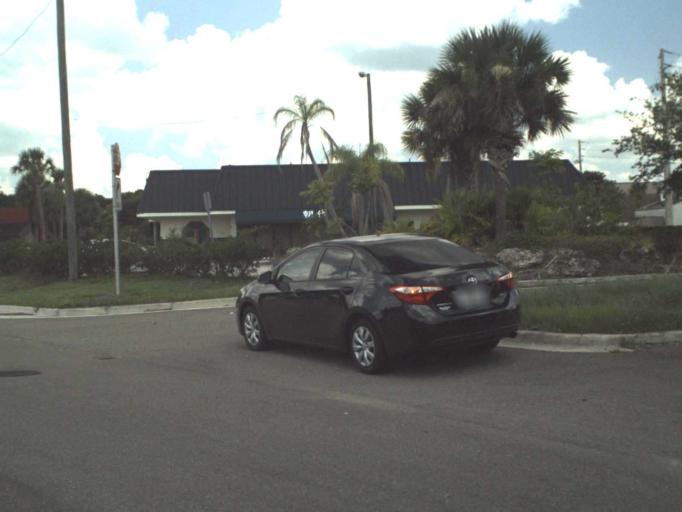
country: US
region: Florida
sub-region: Seminole County
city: Wekiwa Springs
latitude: 28.6900
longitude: -81.3902
